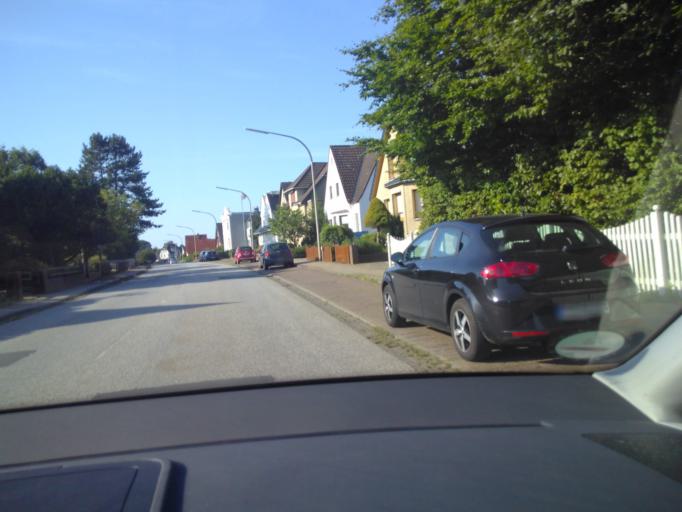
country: DE
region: Lower Saxony
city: Cuxhaven
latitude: 53.8705
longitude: 8.6540
